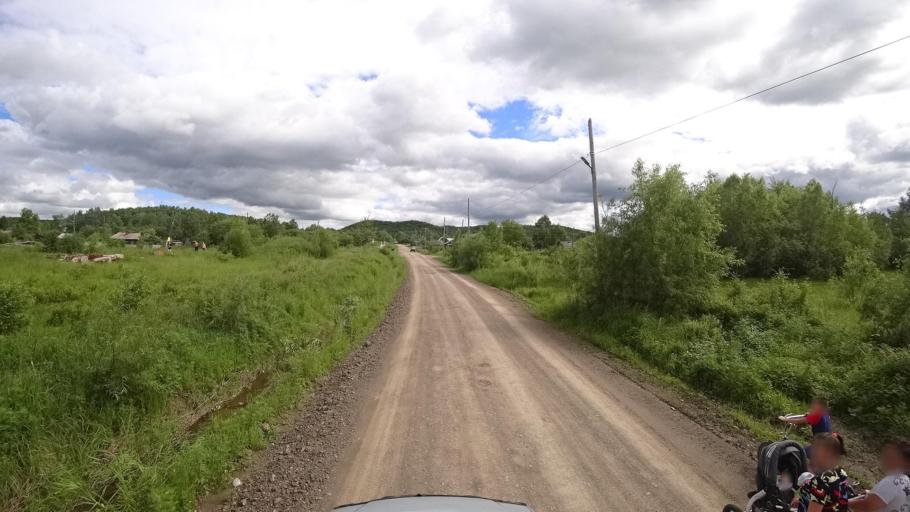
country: RU
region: Khabarovsk Krai
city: Litovko
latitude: 49.3702
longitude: 135.1726
